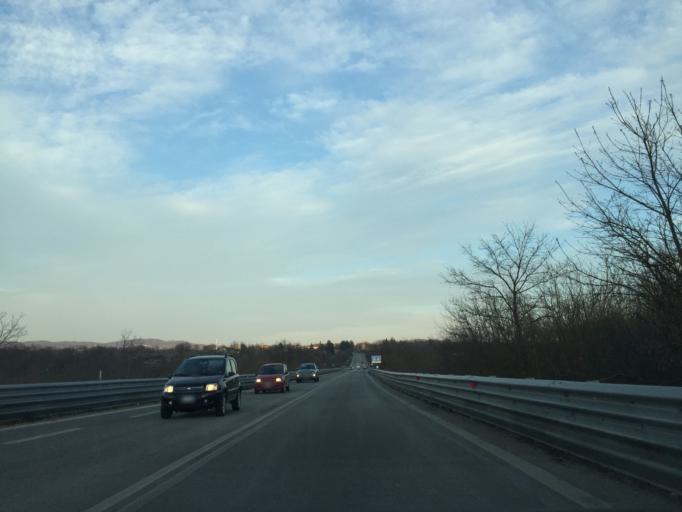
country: IT
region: Molise
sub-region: Provincia di Campobasso
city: Vinchiaturo
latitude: 41.4754
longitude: 14.5616
